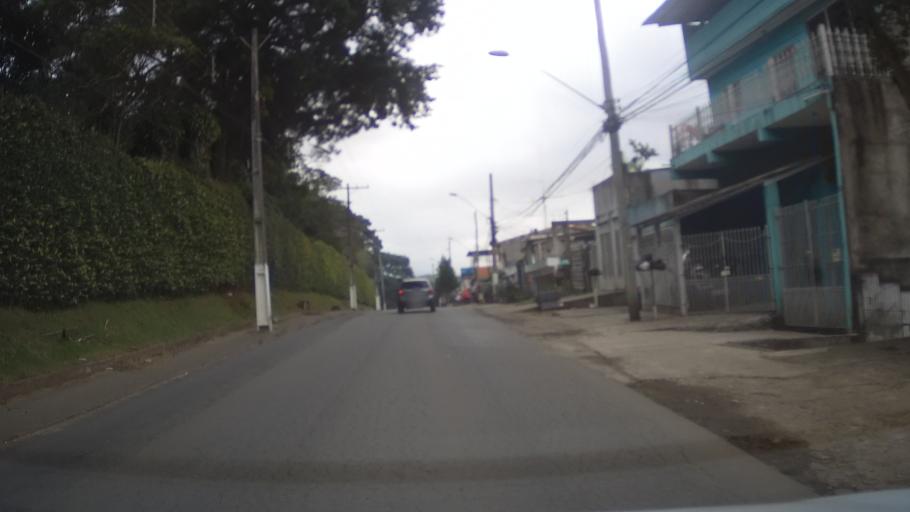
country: BR
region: Sao Paulo
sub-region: Aruja
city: Aruja
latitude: -23.4108
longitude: -46.3732
